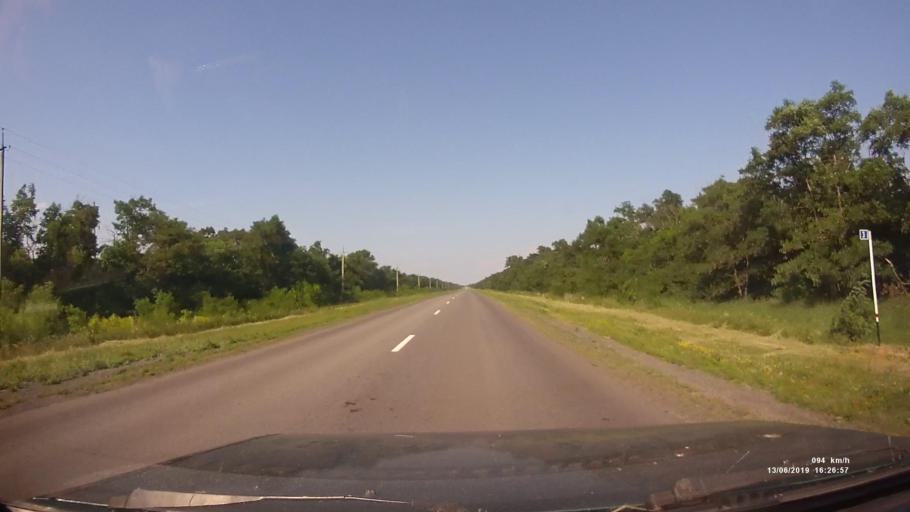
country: RU
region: Rostov
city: Kazanskaya
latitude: 49.8091
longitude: 41.1742
